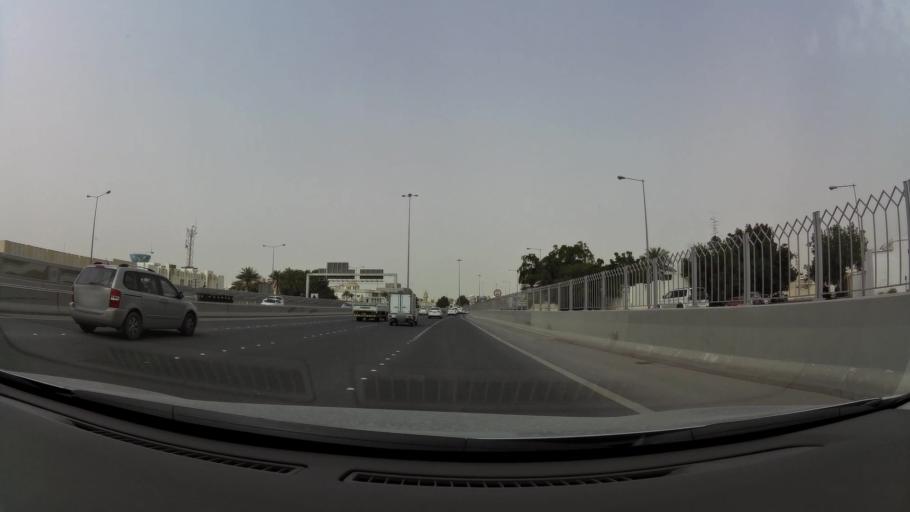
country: QA
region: Baladiyat ad Dawhah
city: Doha
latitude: 25.2568
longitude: 51.5036
